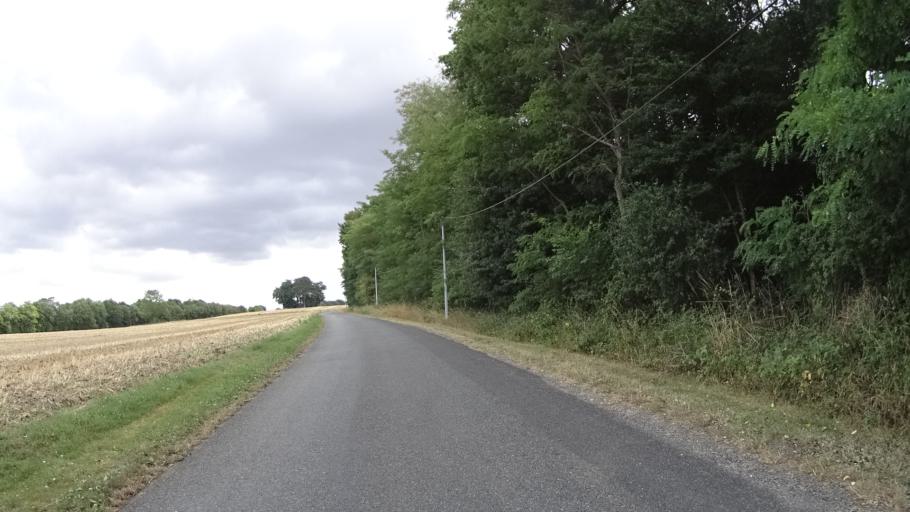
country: FR
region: Centre
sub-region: Departement du Loiret
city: Amilly
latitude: 47.9503
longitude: 2.7940
